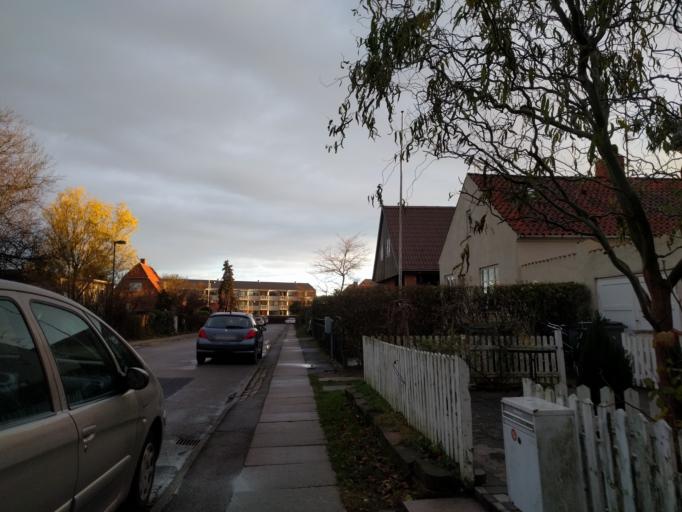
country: DK
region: Capital Region
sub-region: Tarnby Kommune
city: Tarnby
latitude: 55.6456
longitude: 12.6315
